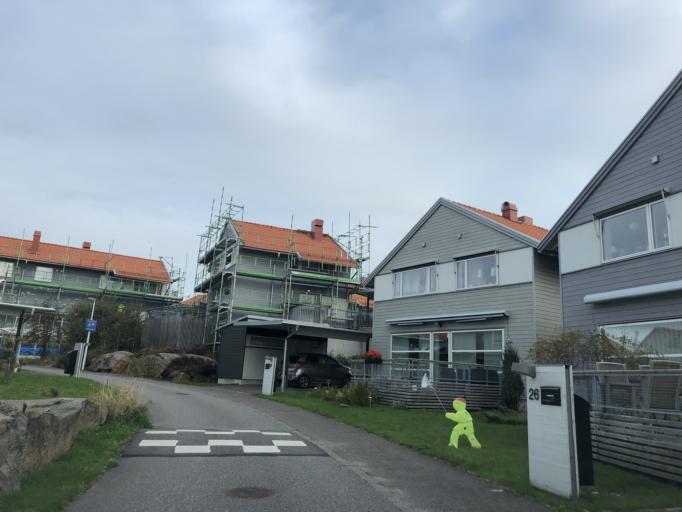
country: SE
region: Vaestra Goetaland
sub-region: Goteborg
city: Majorna
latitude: 57.6811
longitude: 11.8786
